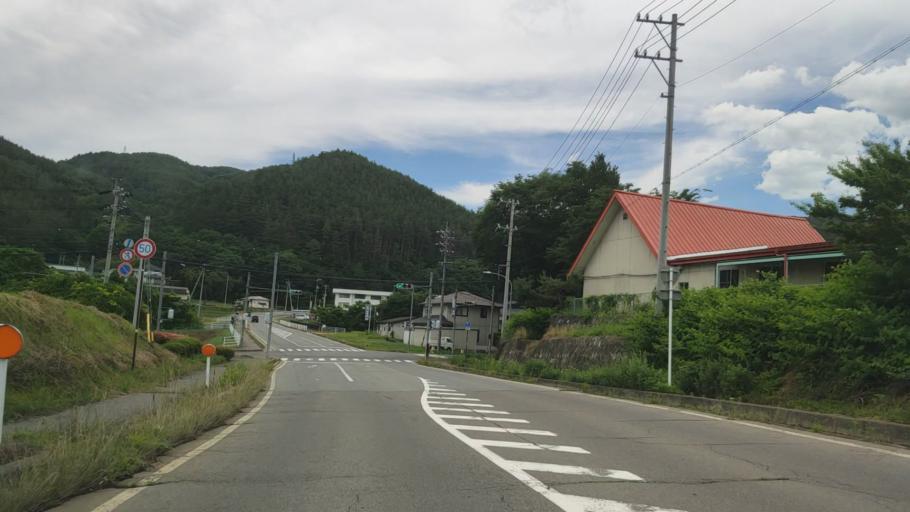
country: JP
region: Nagano
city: Kamimaruko
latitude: 36.2757
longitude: 138.2634
